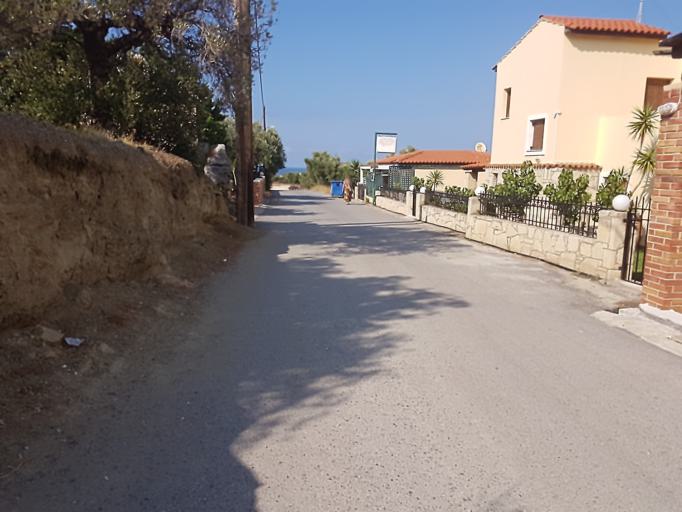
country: GR
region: Crete
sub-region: Nomos Irakleiou
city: Limin Khersonisou
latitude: 35.3160
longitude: 25.3866
